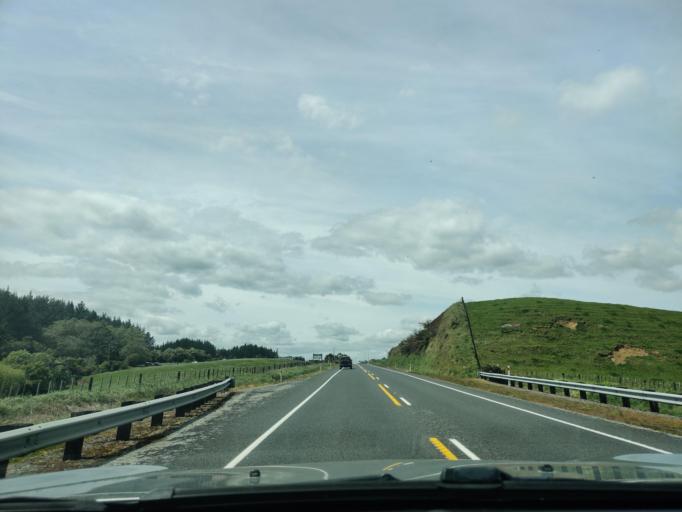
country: NZ
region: Taranaki
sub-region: New Plymouth District
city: New Plymouth
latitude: -39.1335
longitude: 174.1234
